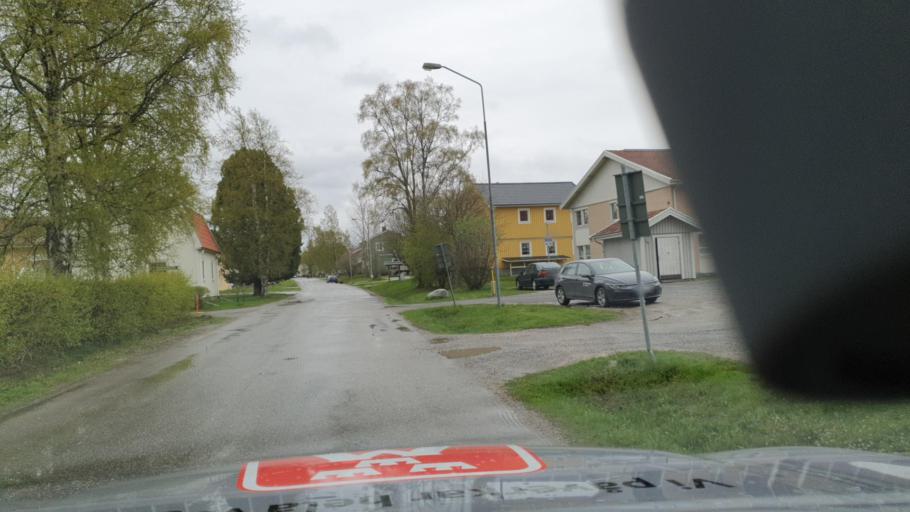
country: SE
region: Vaesternorrland
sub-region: OErnskoeldsviks Kommun
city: Ornskoldsvik
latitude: 63.2728
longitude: 18.6635
